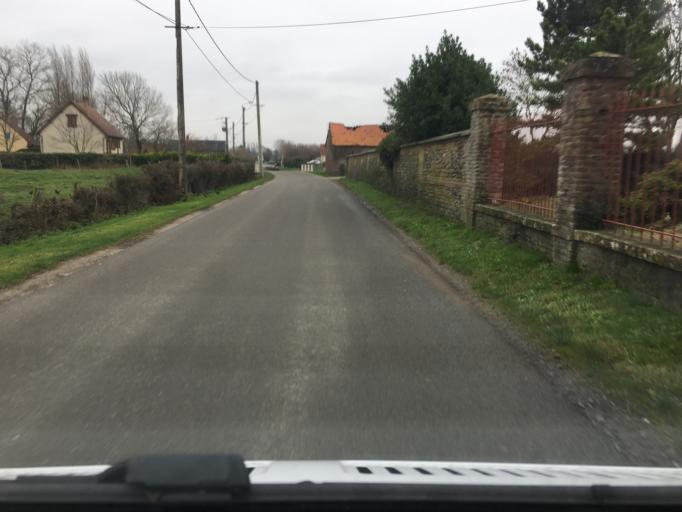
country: FR
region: Picardie
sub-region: Departement de la Somme
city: Pende
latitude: 50.1713
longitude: 1.5474
